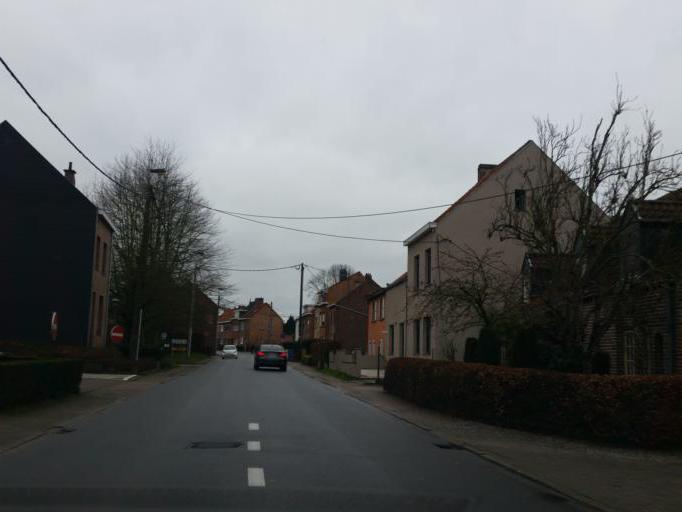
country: BE
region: Flanders
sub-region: Provincie Vlaams-Brabant
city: Grimbergen
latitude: 50.9357
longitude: 4.3829
